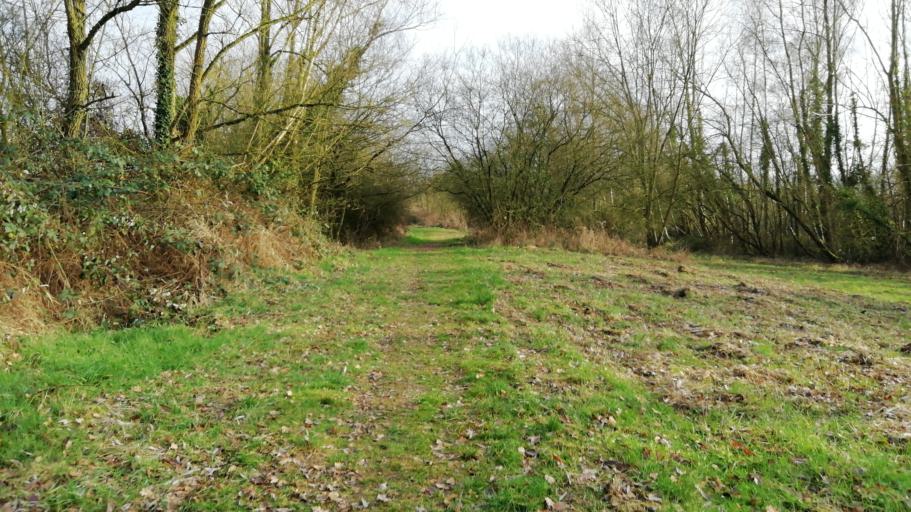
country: FR
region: Nord-Pas-de-Calais
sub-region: Departement du Nord
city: Boussois
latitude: 50.2868
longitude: 4.0498
